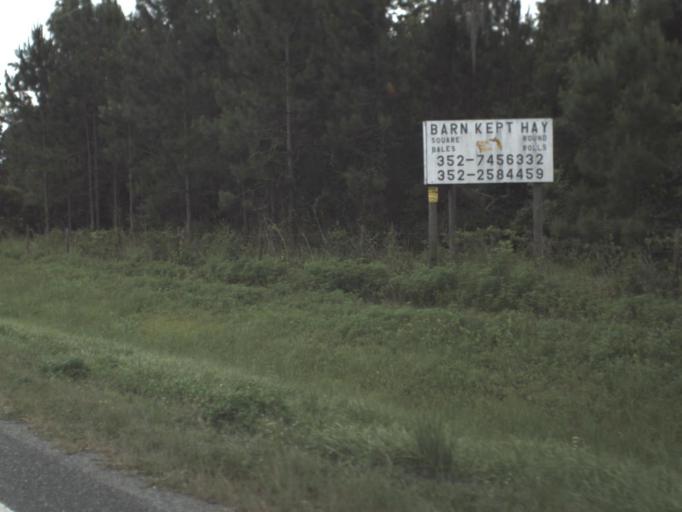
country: US
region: Florida
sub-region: Union County
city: Lake Butler
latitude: 29.9945
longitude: -82.2675
